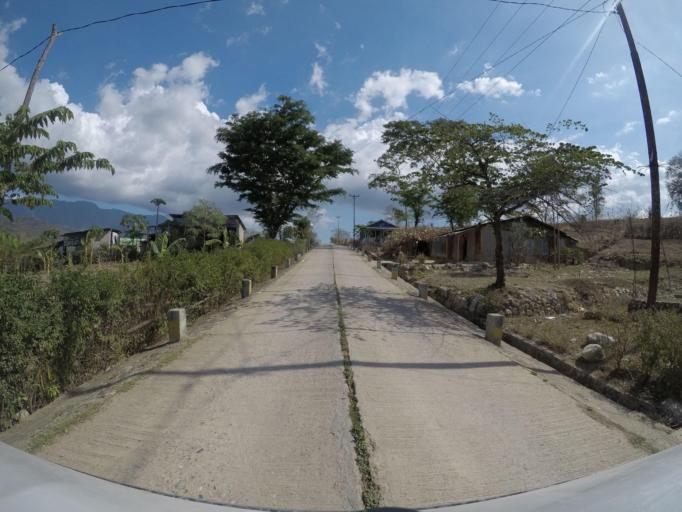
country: TL
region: Bobonaro
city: Maliana
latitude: -8.9997
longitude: 125.1965
